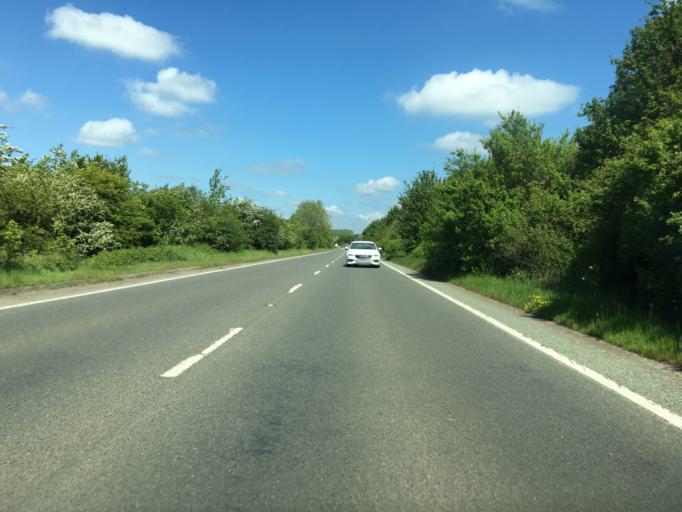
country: GB
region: England
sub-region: Northamptonshire
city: Brackley
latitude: 52.0288
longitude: -1.1613
